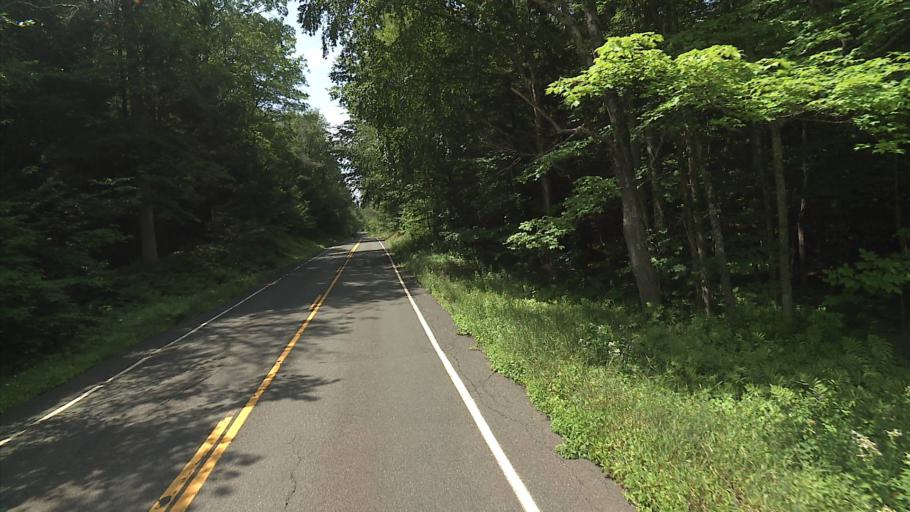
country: US
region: Connecticut
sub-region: Litchfield County
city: Winsted
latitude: 41.9890
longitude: -73.1025
